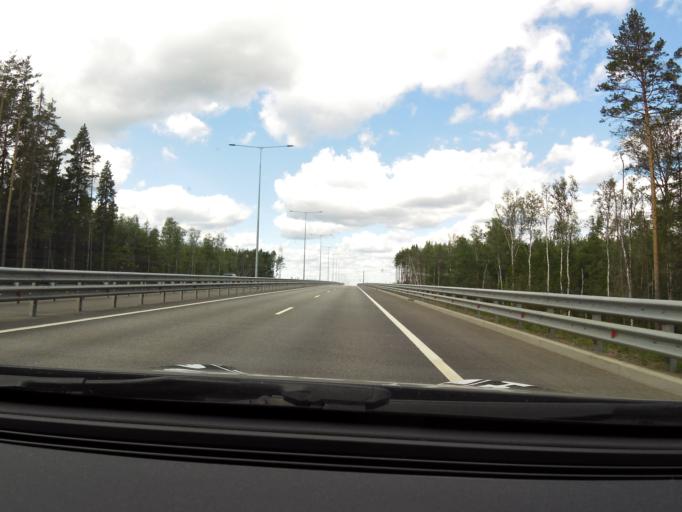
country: RU
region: Tverskaya
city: Vyshniy Volochek
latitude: 57.4325
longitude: 34.4668
